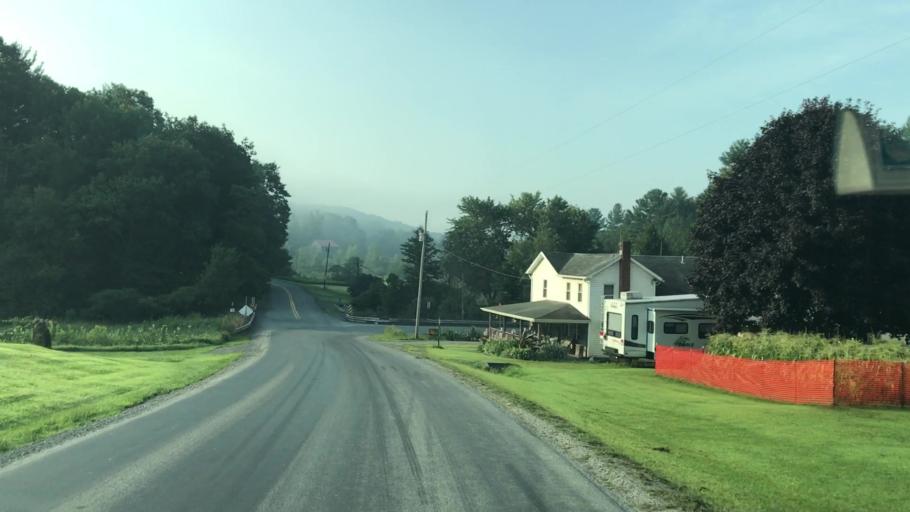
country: US
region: Pennsylvania
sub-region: Wyoming County
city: Factoryville
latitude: 41.6511
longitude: -75.7972
